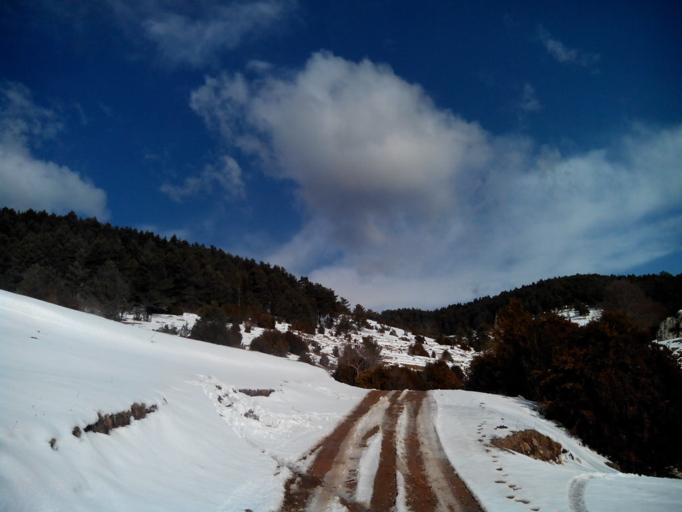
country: ES
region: Catalonia
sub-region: Provincia de Barcelona
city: Sant Julia de Cerdanyola
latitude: 42.1938
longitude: 1.9240
